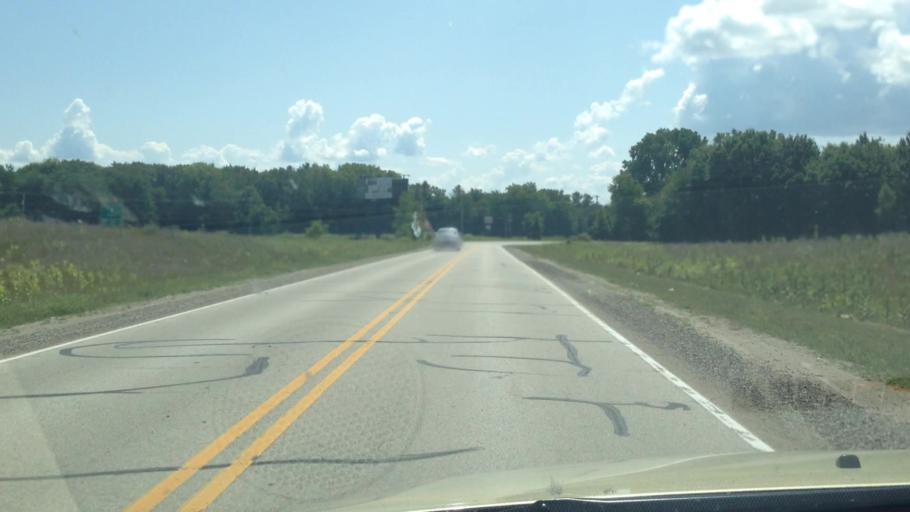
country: US
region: Wisconsin
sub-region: Brown County
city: Suamico
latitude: 44.6545
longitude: -88.0524
